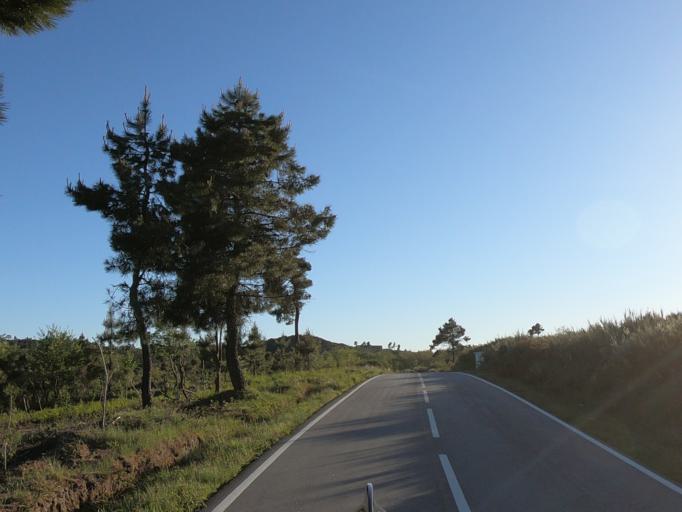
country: PT
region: Vila Real
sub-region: Sabrosa
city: Sabrosa
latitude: 41.3645
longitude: -7.6308
